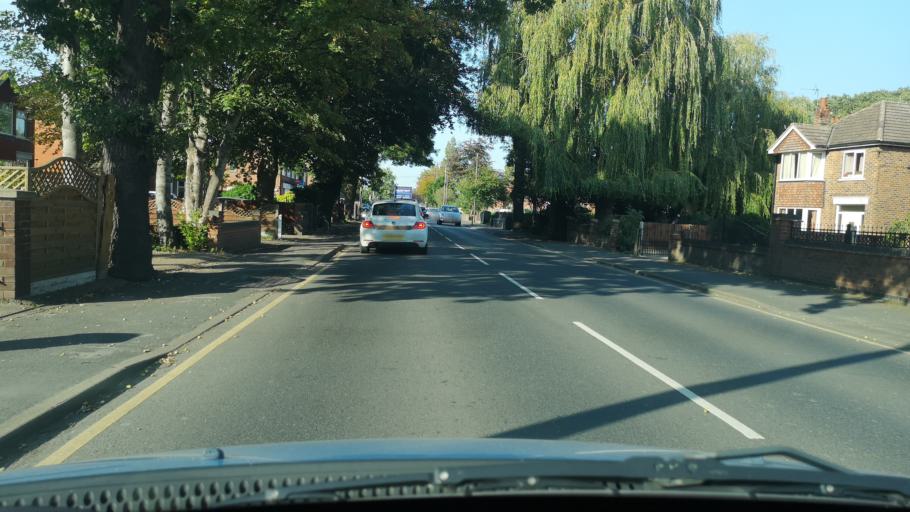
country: GB
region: England
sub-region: North Lincolnshire
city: Scunthorpe
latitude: 53.5877
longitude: -0.6840
